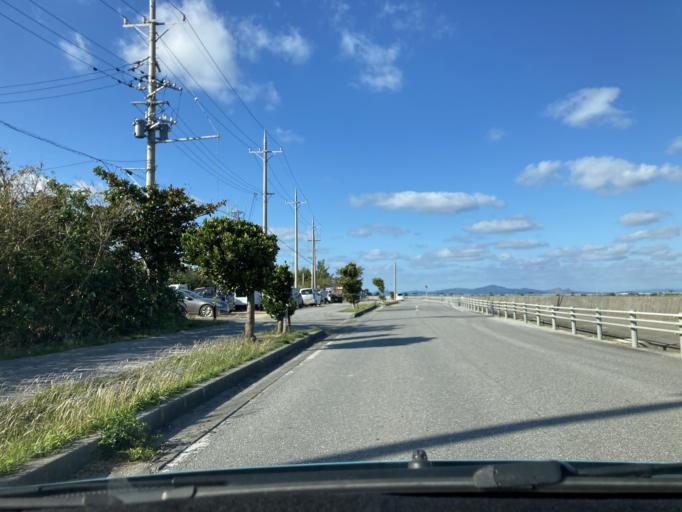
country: JP
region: Okinawa
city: Katsuren-haebaru
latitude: 26.3244
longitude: 127.9129
